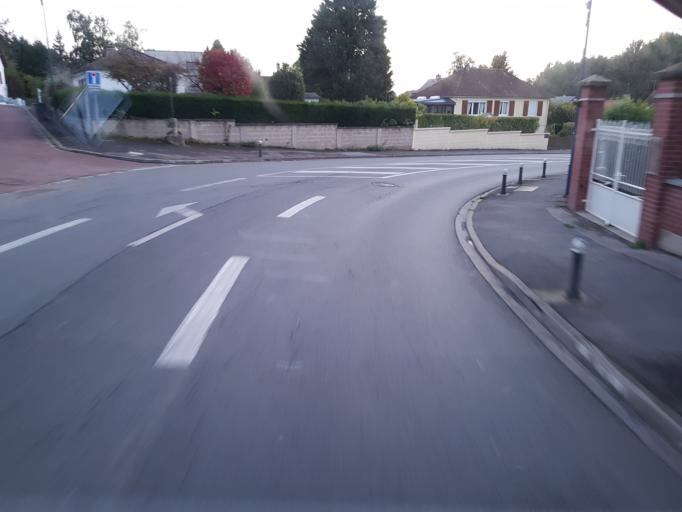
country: FR
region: Picardie
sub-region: Departement de la Somme
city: Ailly-sur-Noye
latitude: 49.7534
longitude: 2.3601
